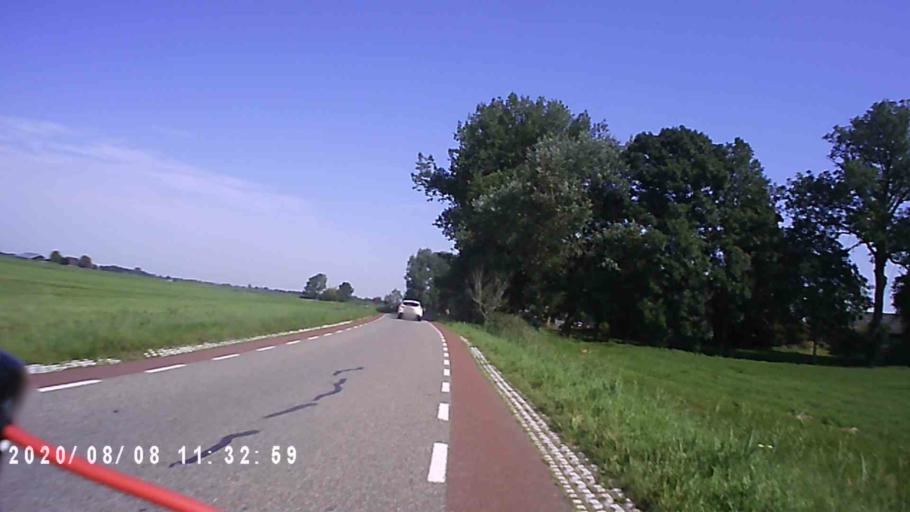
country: NL
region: Groningen
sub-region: Gemeente Zuidhorn
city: Zuidhorn
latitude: 53.2112
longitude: 6.3892
